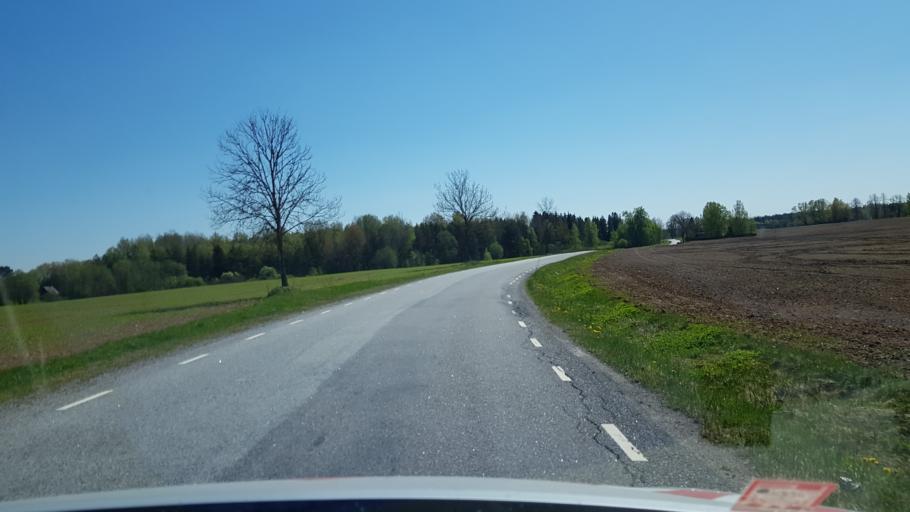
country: EE
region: Vorumaa
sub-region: Voru linn
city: Voru
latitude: 57.9178
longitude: 26.9538
